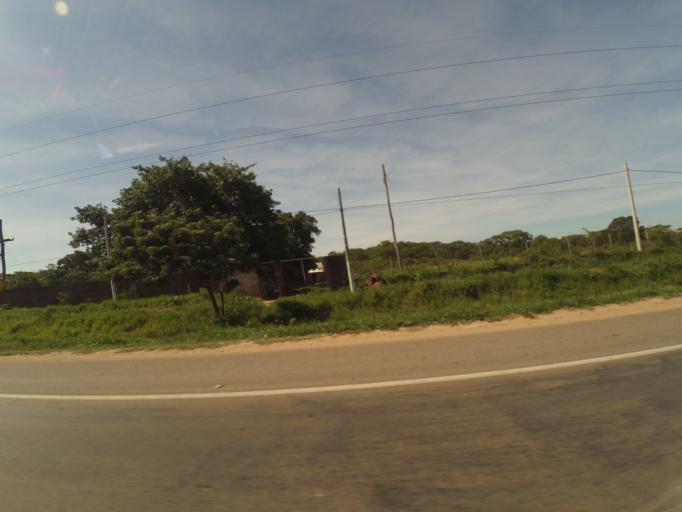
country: BO
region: Santa Cruz
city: Cotoca
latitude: -17.7665
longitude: -63.0565
